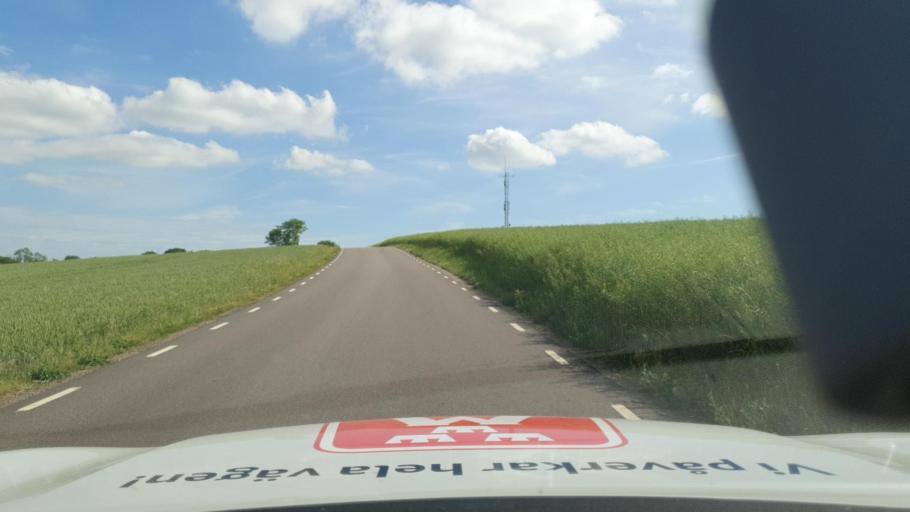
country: SE
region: Skane
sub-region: Sjobo Kommun
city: Blentarp
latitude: 55.5494
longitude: 13.5591
